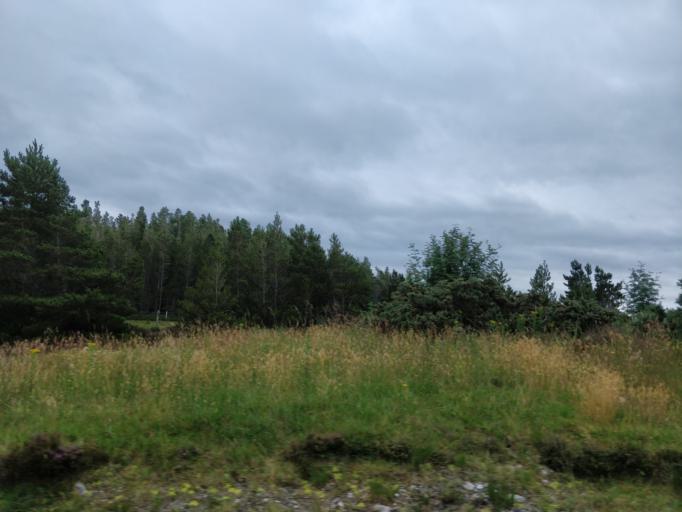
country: GB
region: Scotland
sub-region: Highland
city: Ullapool
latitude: 57.9140
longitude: -5.1850
